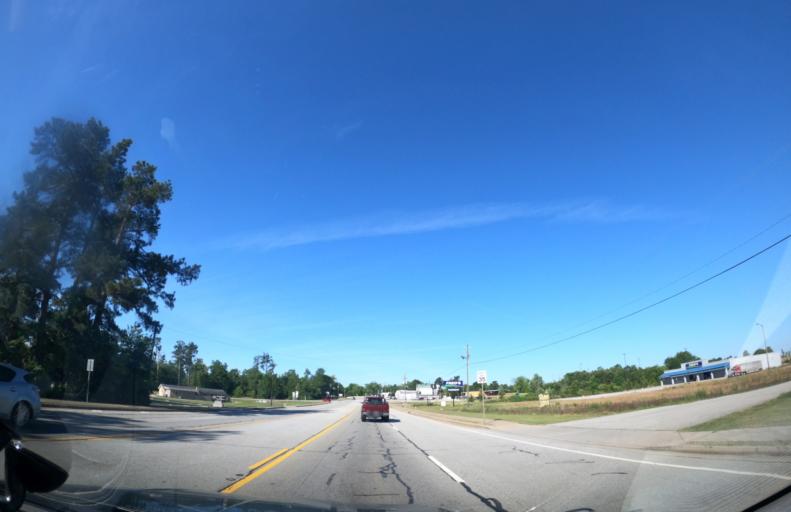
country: US
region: Georgia
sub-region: Jefferson County
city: Wrens
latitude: 33.2171
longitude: -82.3806
